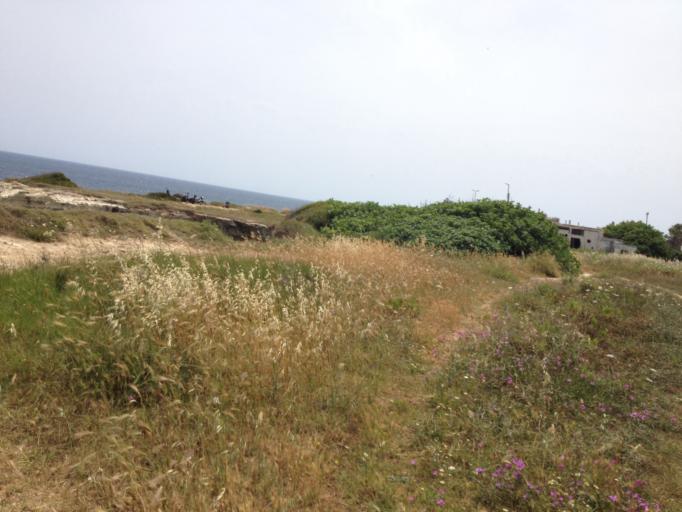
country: IT
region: Apulia
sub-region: Provincia di Lecce
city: Borgagne
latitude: 40.2571
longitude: 18.4430
